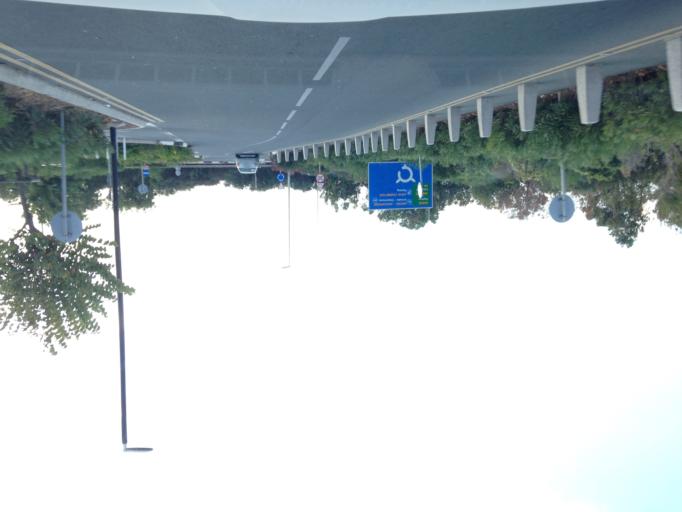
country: CY
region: Pafos
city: Paphos
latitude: 34.7104
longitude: 32.4905
